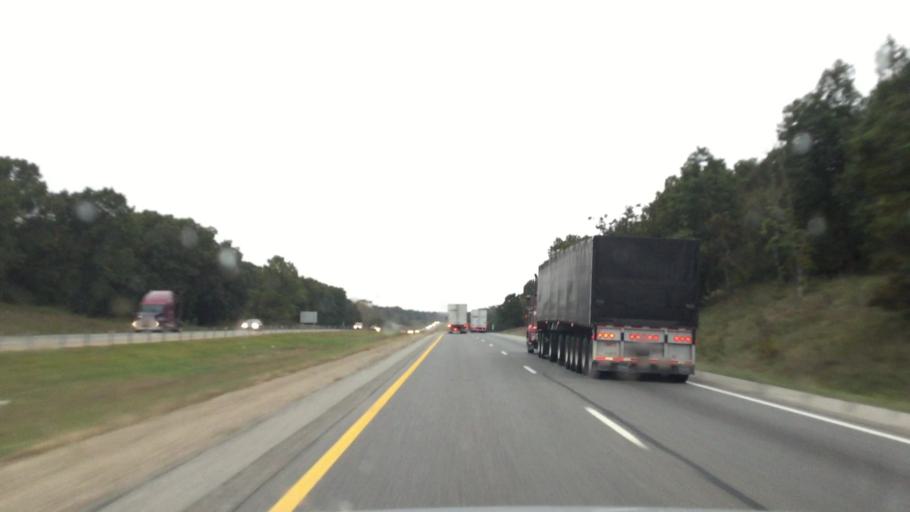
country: US
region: Michigan
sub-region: Van Buren County
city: Mattawan
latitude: 42.2335
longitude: -85.7119
